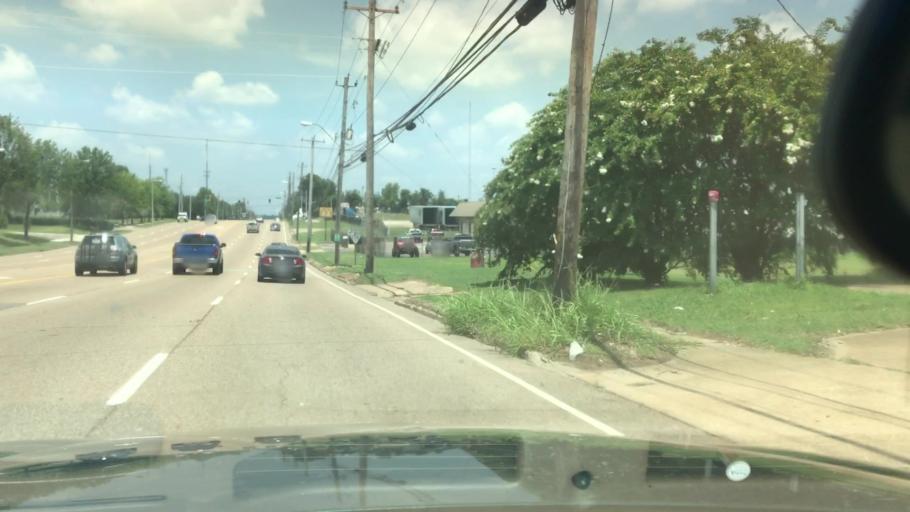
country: US
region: Mississippi
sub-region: De Soto County
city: Southaven
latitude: 35.0217
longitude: -89.9368
